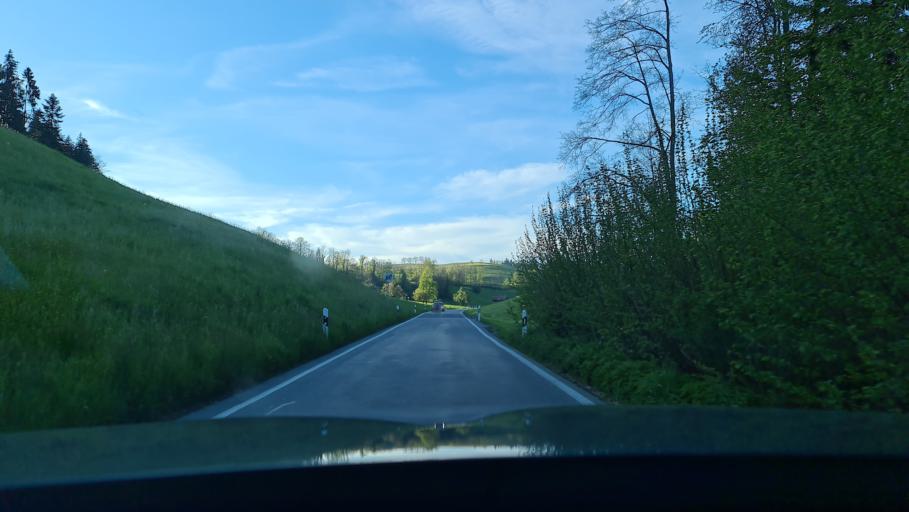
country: CH
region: Lucerne
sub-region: Entlebuch District
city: Wolhusen
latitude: 47.0602
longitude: 8.0894
